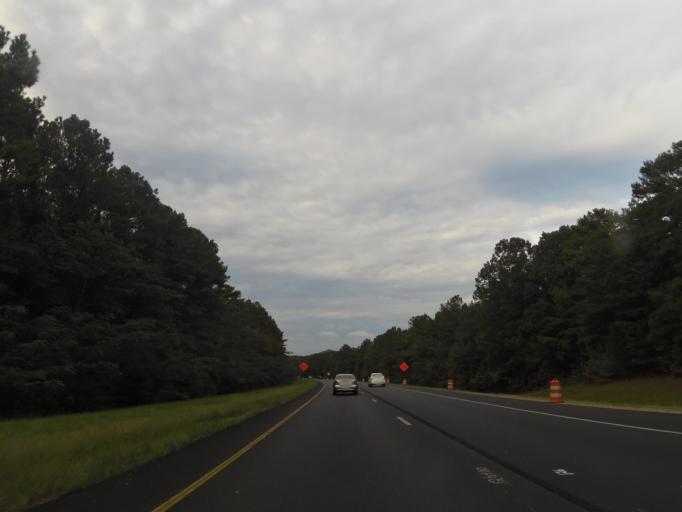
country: US
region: Alabama
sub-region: Shelby County
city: Alabaster
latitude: 33.2442
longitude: -86.7996
